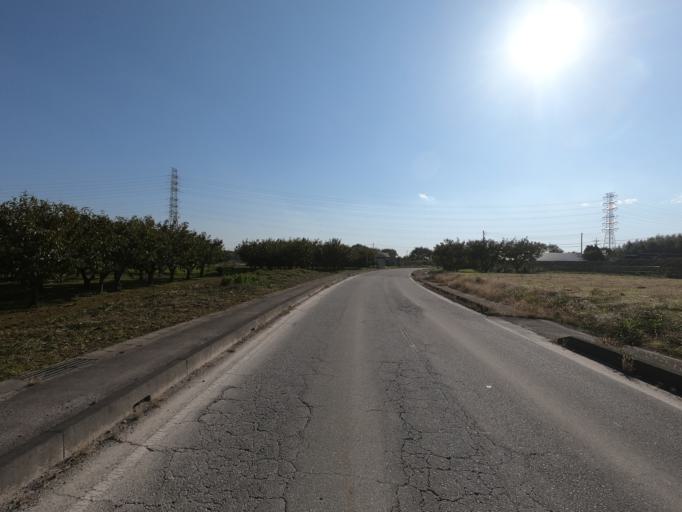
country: JP
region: Ibaraki
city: Tsukuba
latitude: 36.1426
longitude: 140.1511
